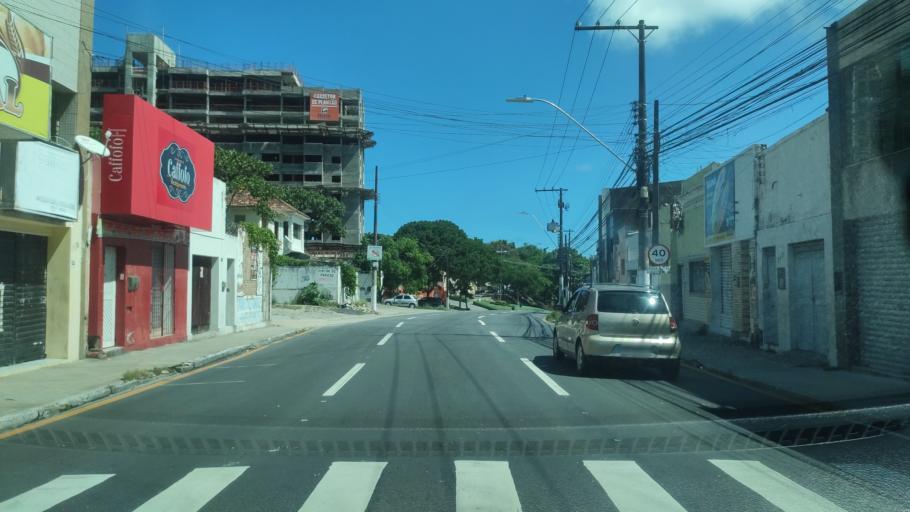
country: BR
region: Alagoas
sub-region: Maceio
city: Maceio
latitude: -9.6582
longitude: -35.7360
